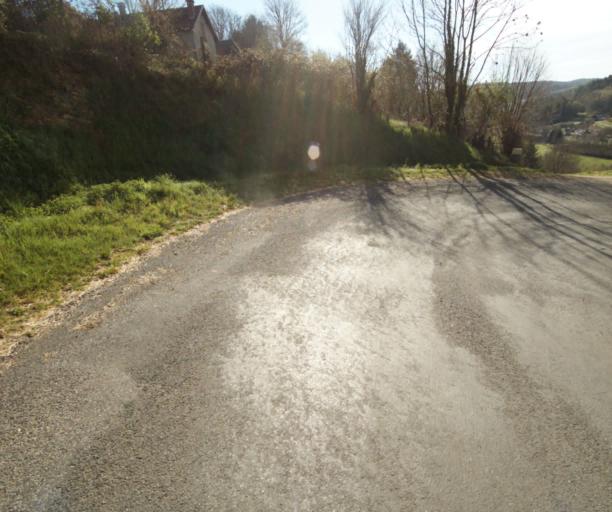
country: FR
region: Limousin
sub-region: Departement de la Correze
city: Laguenne
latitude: 45.2566
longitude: 1.8340
